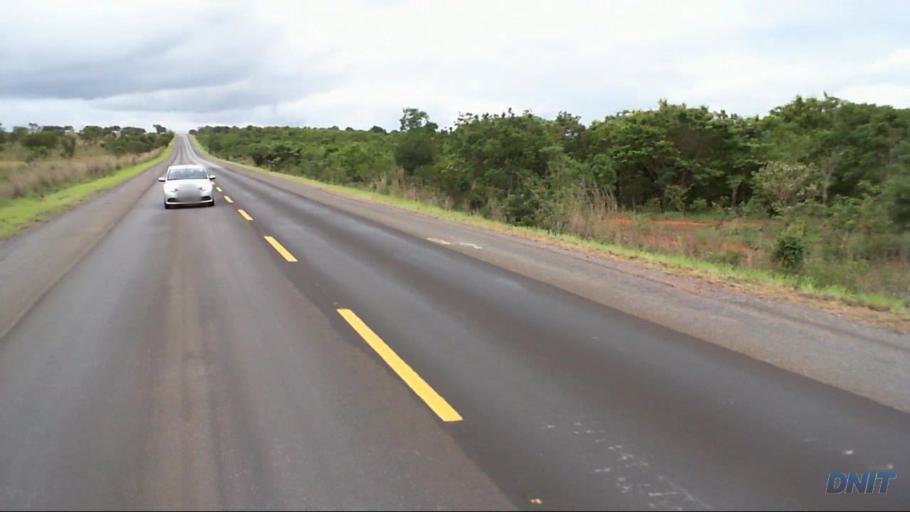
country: BR
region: Goias
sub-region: Padre Bernardo
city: Padre Bernardo
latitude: -15.2182
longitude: -48.5527
